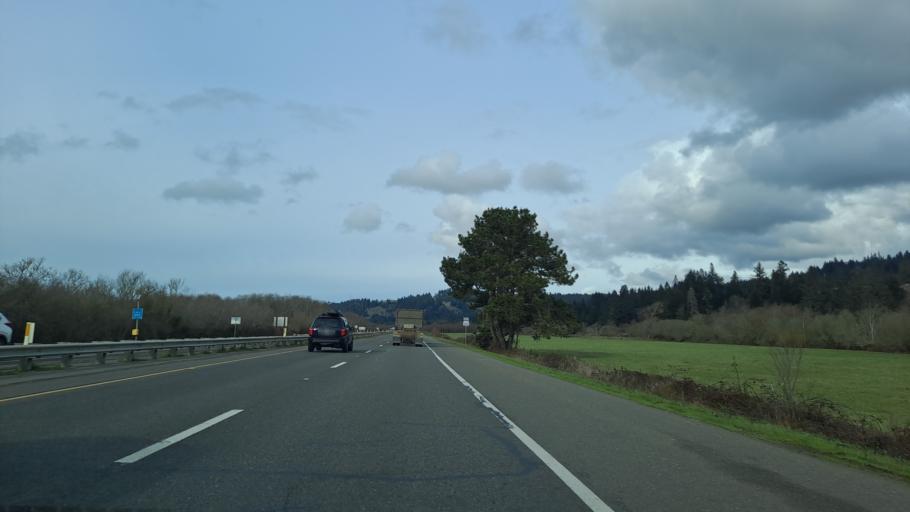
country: US
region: California
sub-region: Humboldt County
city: Humboldt Hill
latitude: 40.6730
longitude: -124.2015
